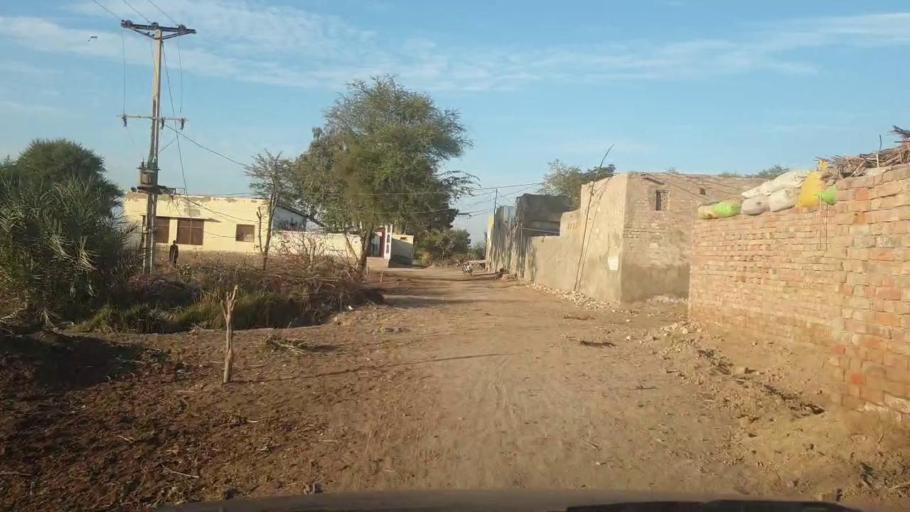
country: PK
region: Sindh
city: Sinjhoro
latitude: 26.0379
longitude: 68.8349
